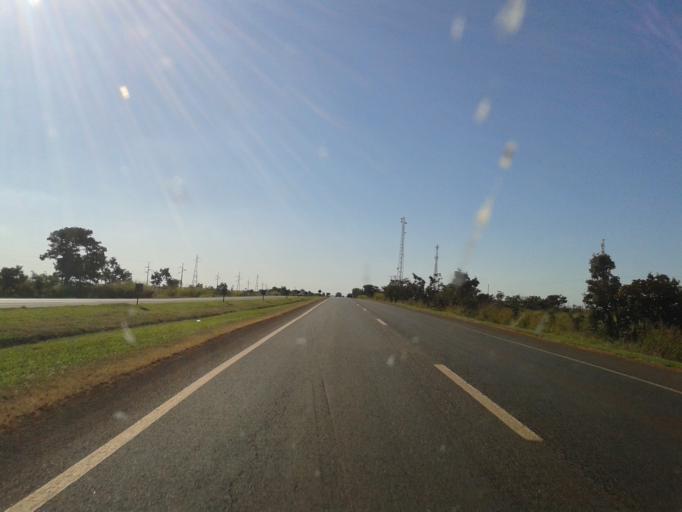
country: BR
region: Minas Gerais
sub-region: Uberlandia
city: Uberlandia
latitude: -19.0752
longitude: -48.1889
